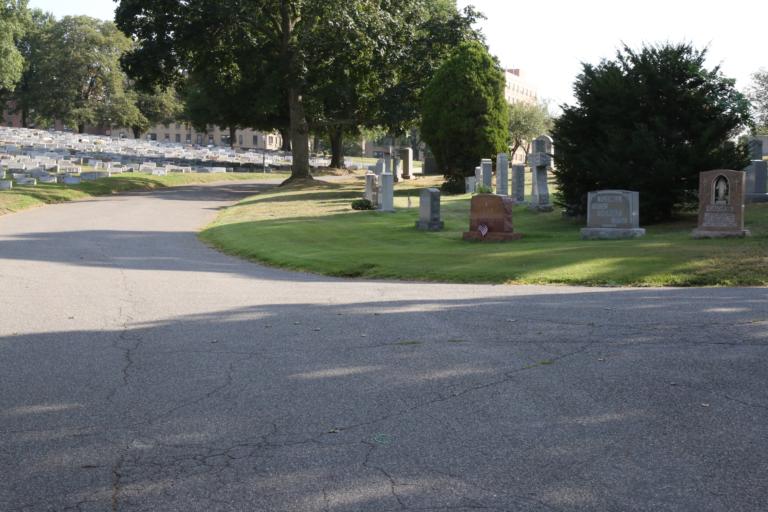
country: US
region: New York
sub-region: Bronx
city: The Bronx
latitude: 40.8823
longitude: -73.8736
